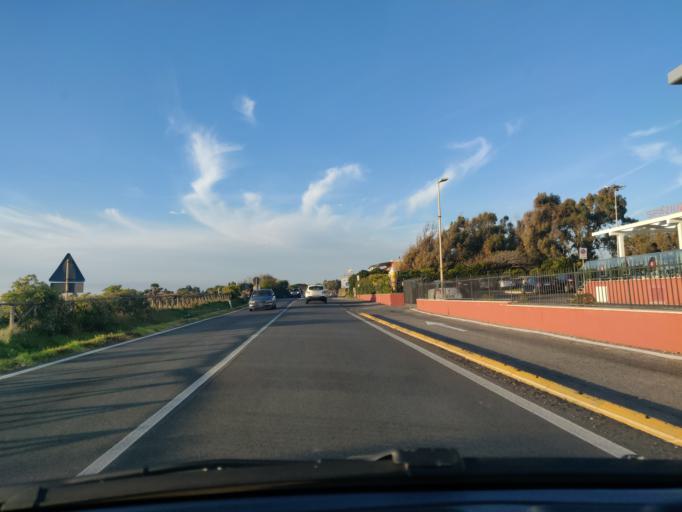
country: IT
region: Latium
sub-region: Citta metropolitana di Roma Capitale
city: Civitavecchia
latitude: 42.0534
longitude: 11.8203
